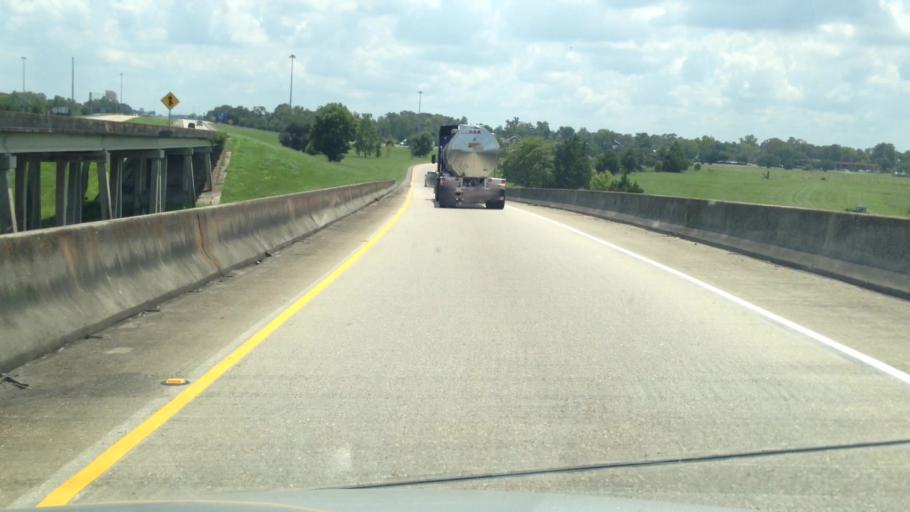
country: US
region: Louisiana
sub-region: Saint Landry Parish
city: Opelousas
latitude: 30.5364
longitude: -92.0646
